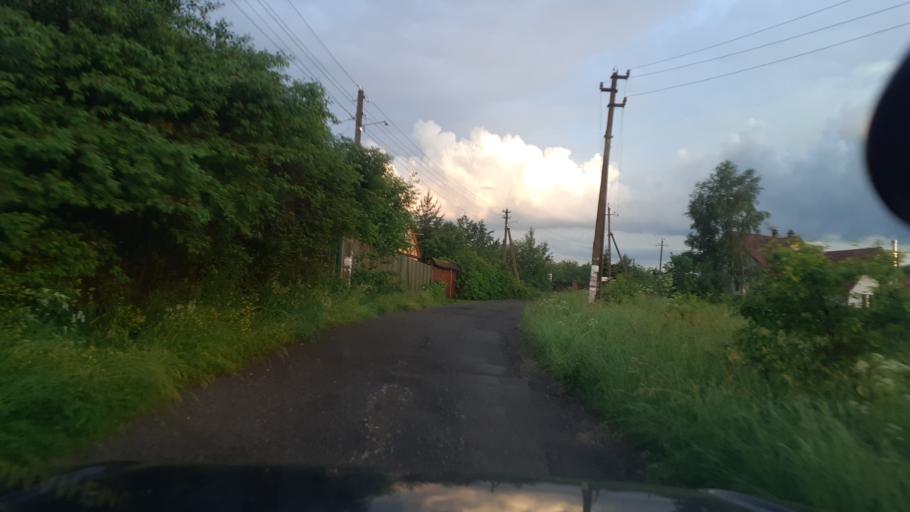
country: RU
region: Moskovskaya
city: Ateptsevo
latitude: 55.2988
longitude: 36.7704
